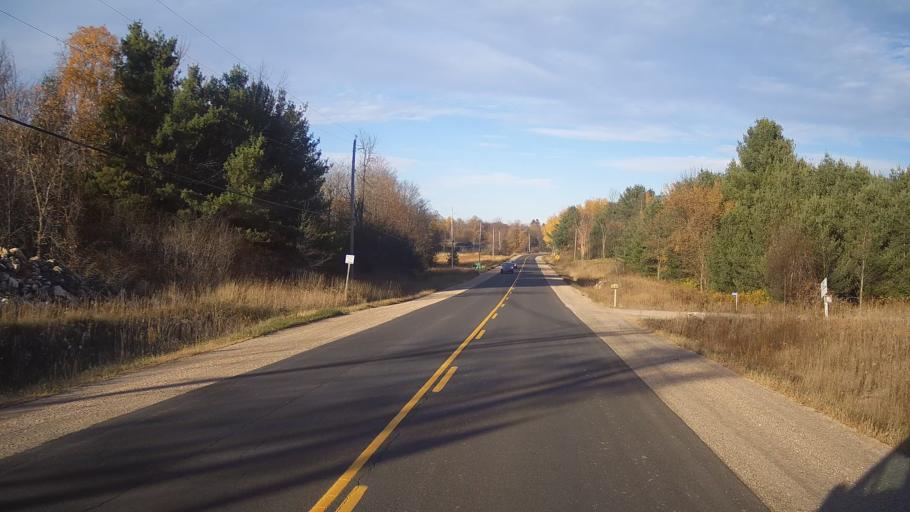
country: CA
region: Ontario
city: Perth
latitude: 44.8110
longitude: -76.3277
